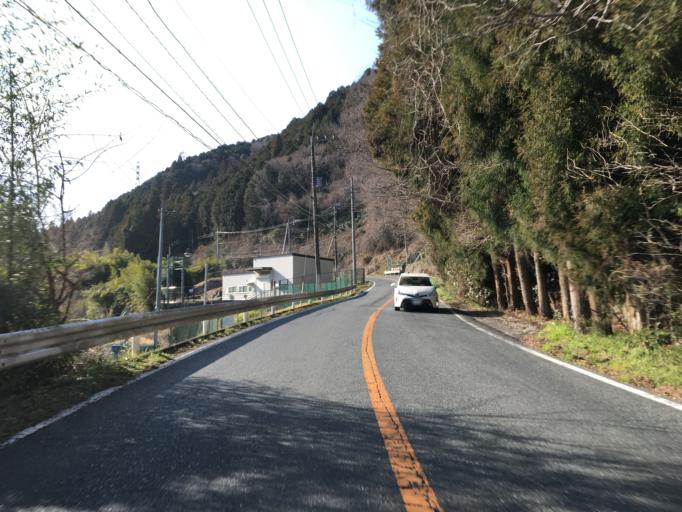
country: JP
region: Ibaraki
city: Takahagi
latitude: 36.7249
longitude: 140.6671
